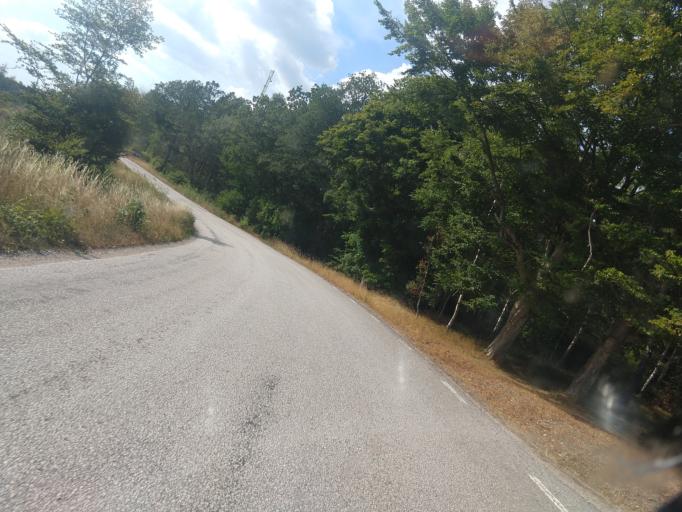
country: SE
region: Blekinge
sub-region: Karlskrona Kommun
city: Rodeby
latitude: 56.2383
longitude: 15.5727
